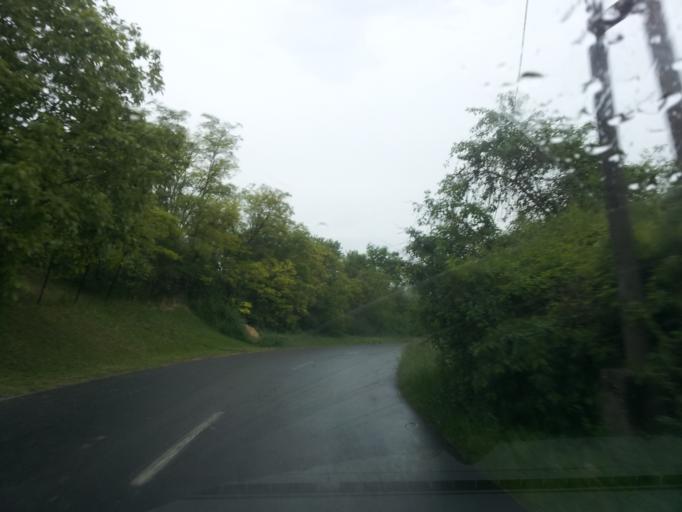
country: HU
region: Tolna
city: Szekszard
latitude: 46.2974
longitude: 18.6827
